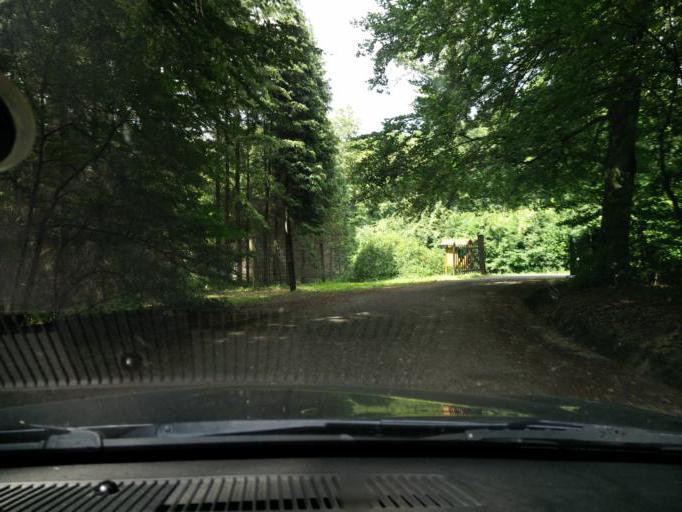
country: HU
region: Komarom-Esztergom
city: Tardos
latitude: 47.6600
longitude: 18.4171
